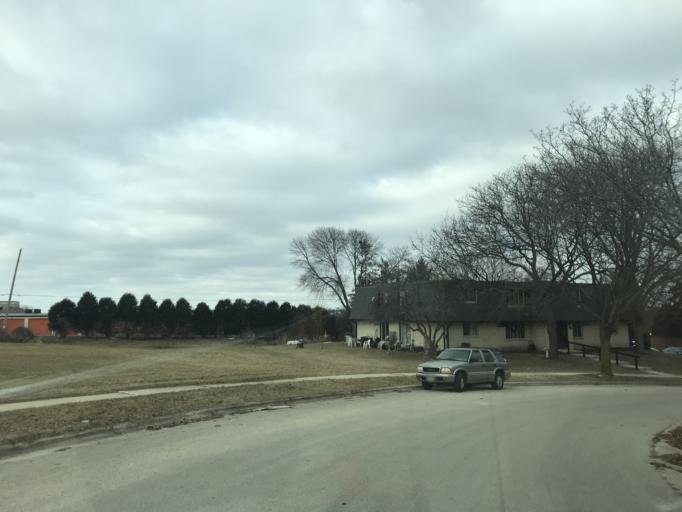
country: US
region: Wisconsin
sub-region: Dane County
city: Monona
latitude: 43.1079
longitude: -89.3071
